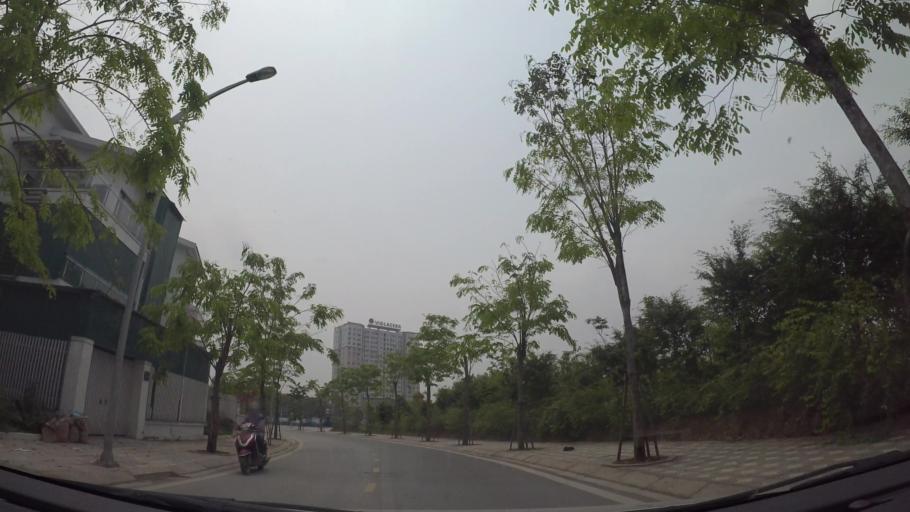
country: VN
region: Ha Noi
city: Cau Dien
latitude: 21.0265
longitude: 105.7434
